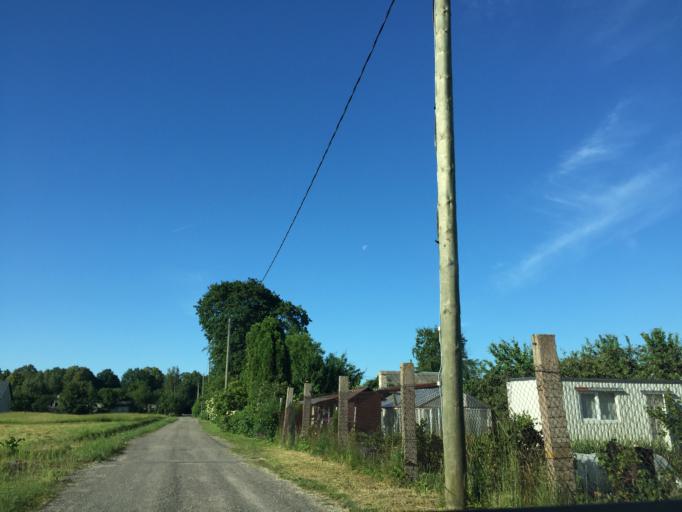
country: LV
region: Ventspils
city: Ventspils
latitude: 57.3659
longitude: 21.6001
